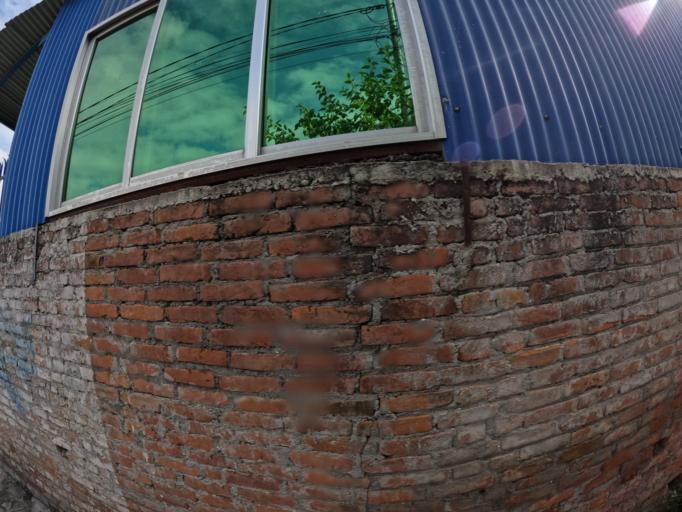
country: NP
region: Central Region
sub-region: Bagmati Zone
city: Kathmandu
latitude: 27.7649
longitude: 85.3318
